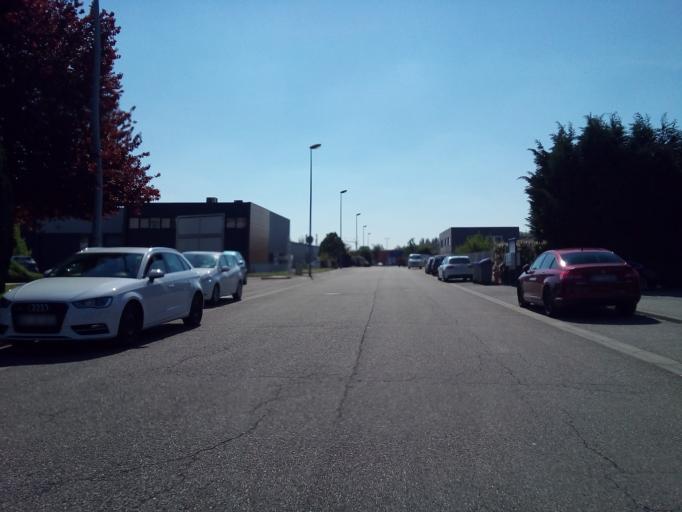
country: FR
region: Alsace
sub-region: Departement du Bas-Rhin
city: Hoenheim
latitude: 48.6327
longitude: 7.7667
